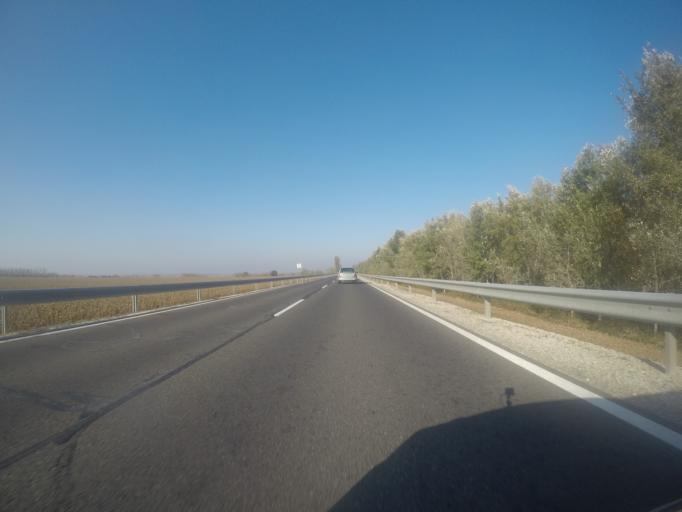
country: HU
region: Fejer
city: Ivancsa
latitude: 47.1857
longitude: 18.8699
